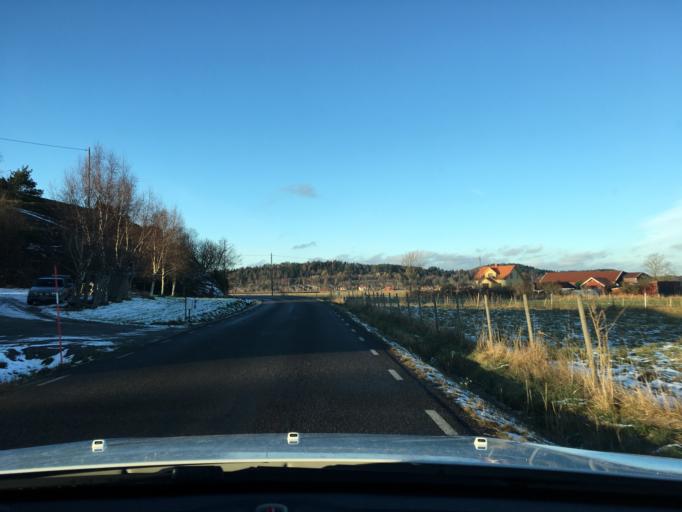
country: SE
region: Vaestra Goetaland
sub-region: Tjorns Kommun
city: Myggenas
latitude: 58.0450
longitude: 11.7291
